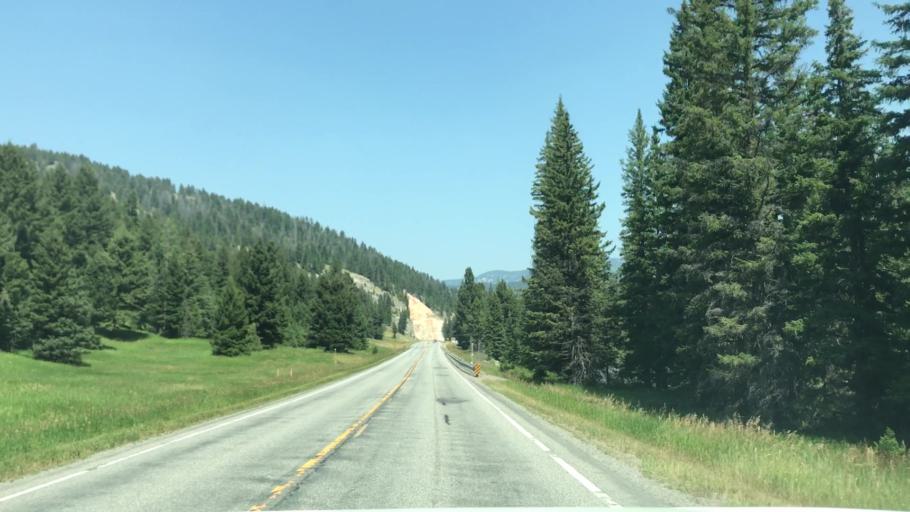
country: US
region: Montana
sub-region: Gallatin County
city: Big Sky
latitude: 45.1703
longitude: -111.2437
